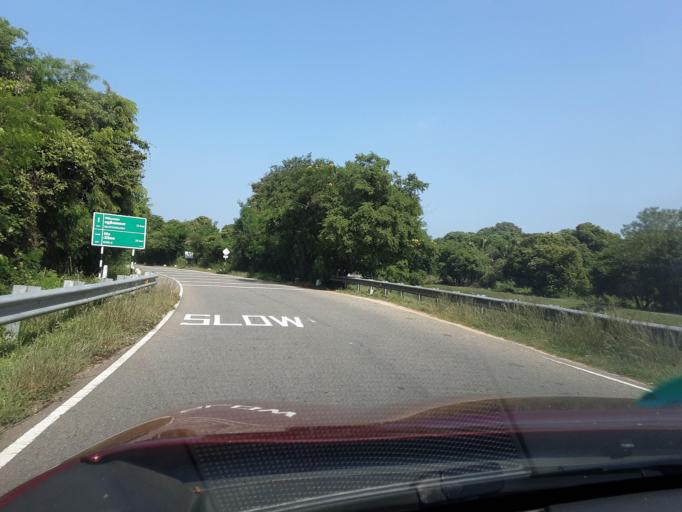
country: LK
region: Uva
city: Badulla
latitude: 7.2818
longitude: 81.0442
